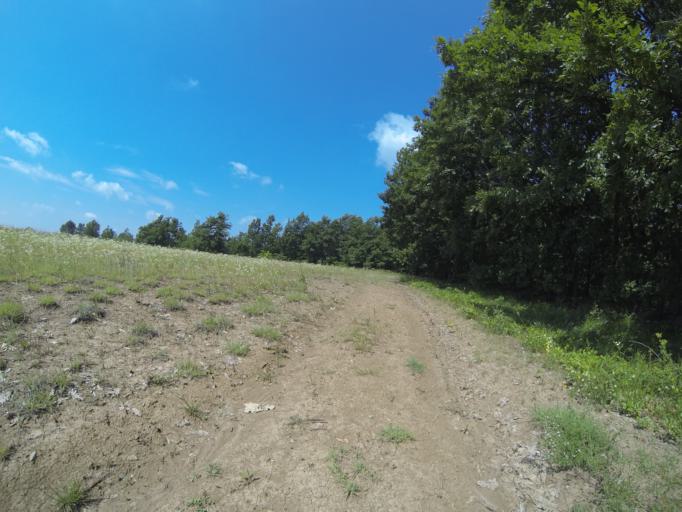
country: RO
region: Gorj
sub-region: Comuna Crusetu
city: Crusetu
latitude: 44.6141
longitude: 23.6323
